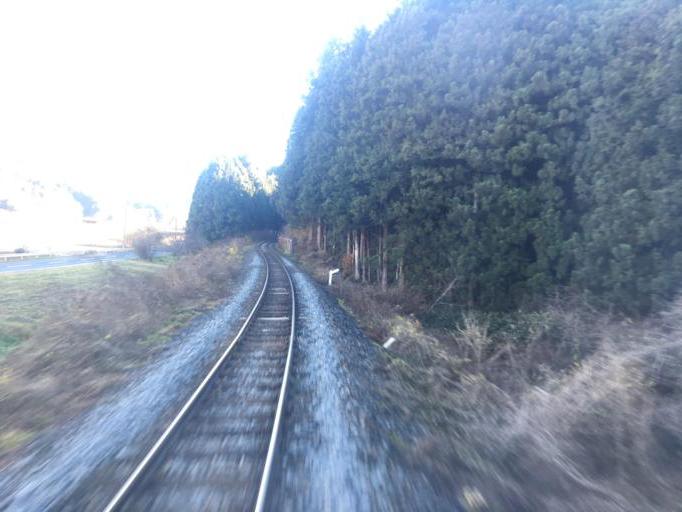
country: JP
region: Iwate
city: Ichinoseki
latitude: 38.9578
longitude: 141.2462
